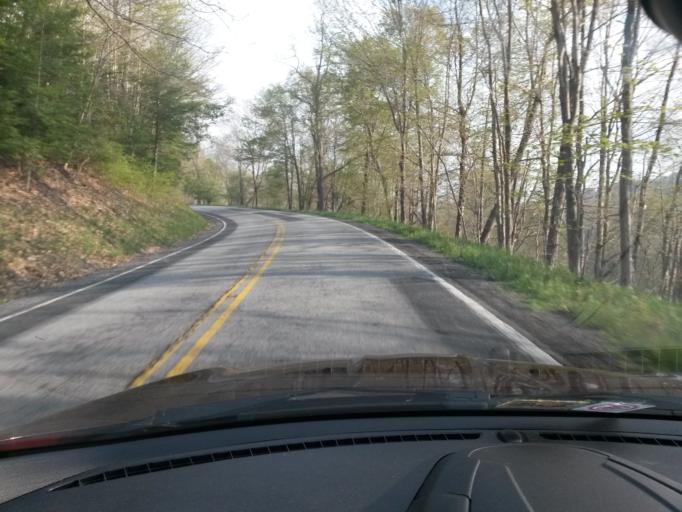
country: US
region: Virginia
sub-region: Highland County
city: Monterey
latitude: 38.4605
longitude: -79.6741
